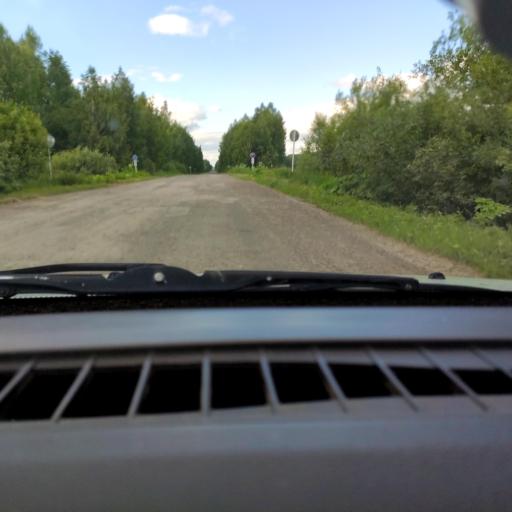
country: RU
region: Perm
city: Kukushtan
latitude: 57.2680
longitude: 56.5342
